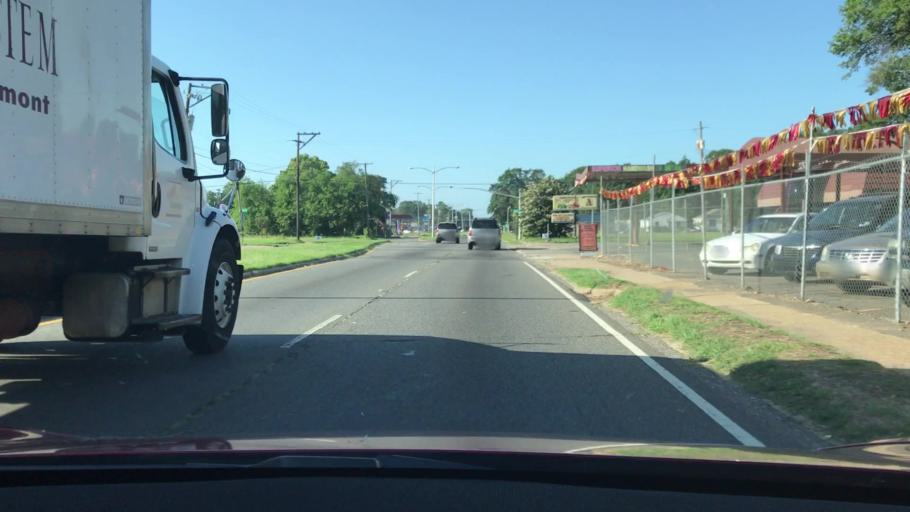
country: US
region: Louisiana
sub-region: Caddo Parish
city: Shreveport
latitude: 32.4753
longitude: -93.7801
